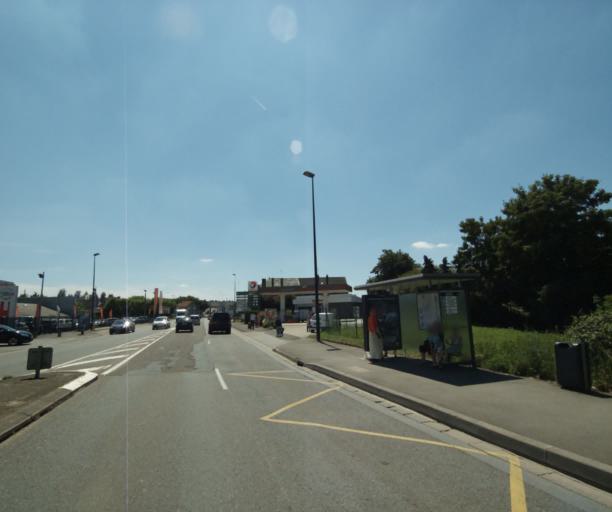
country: FR
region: Pays de la Loire
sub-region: Departement de la Mayenne
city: Laval
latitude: 48.0775
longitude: -0.7529
